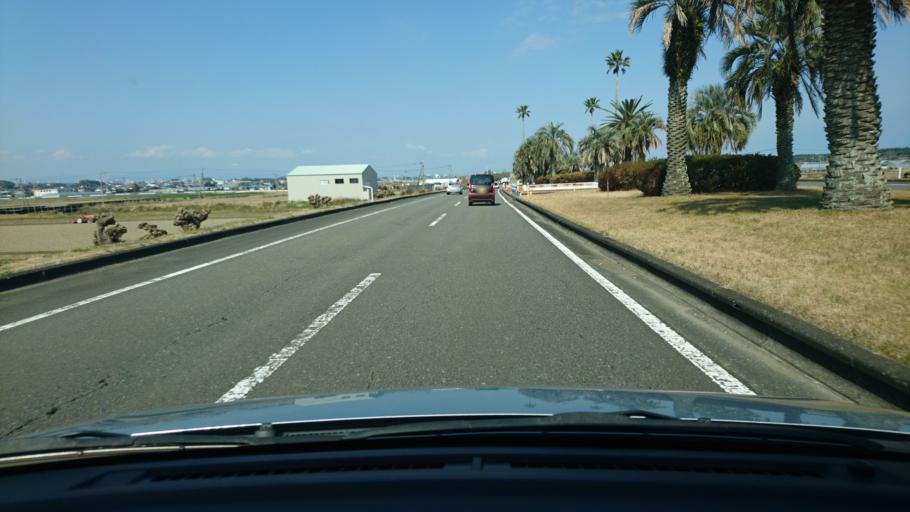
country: JP
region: Miyazaki
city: Miyazaki-shi
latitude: 31.8434
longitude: 131.4443
